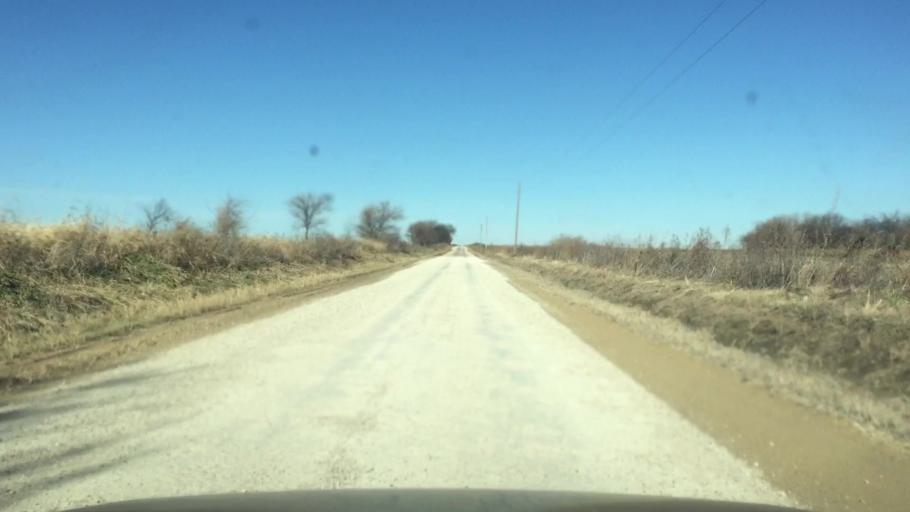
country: US
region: Kansas
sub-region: Allen County
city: Humboldt
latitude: 37.8523
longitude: -95.3909
